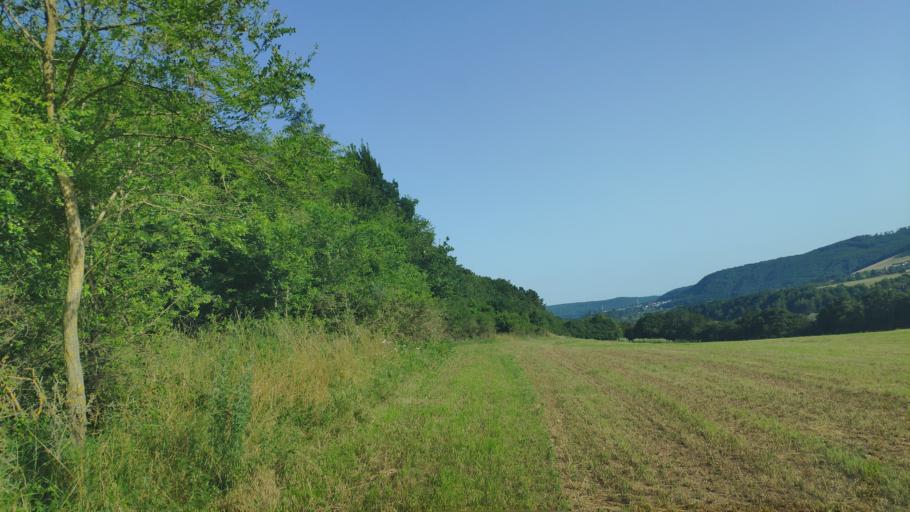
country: SK
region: Kosicky
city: Kosice
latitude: 48.8289
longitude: 21.2259
